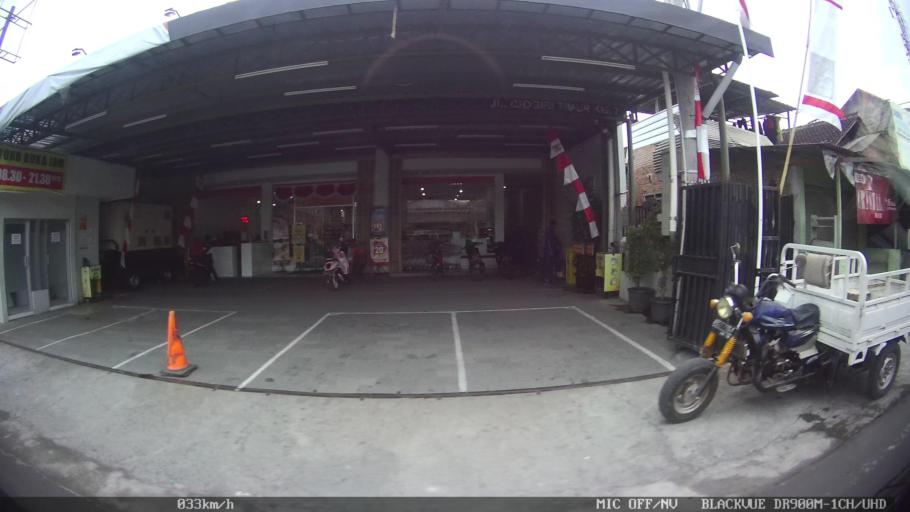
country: ID
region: Daerah Istimewa Yogyakarta
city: Sewon
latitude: -7.8441
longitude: 110.3911
